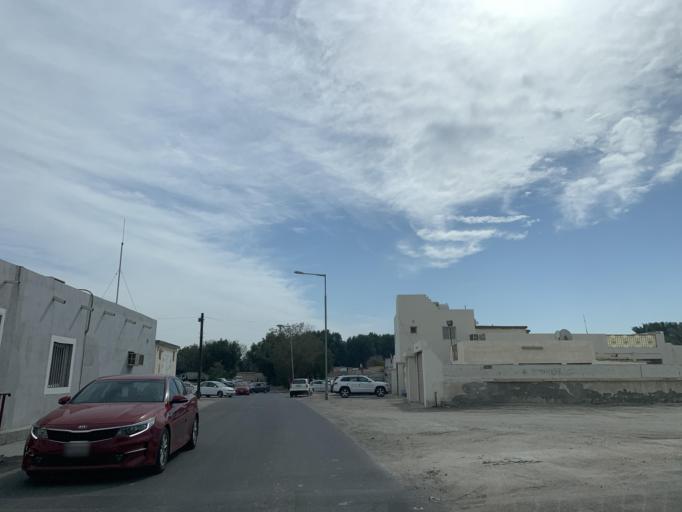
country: BH
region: Central Governorate
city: Madinat Hamad
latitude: 26.1134
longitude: 50.4808
